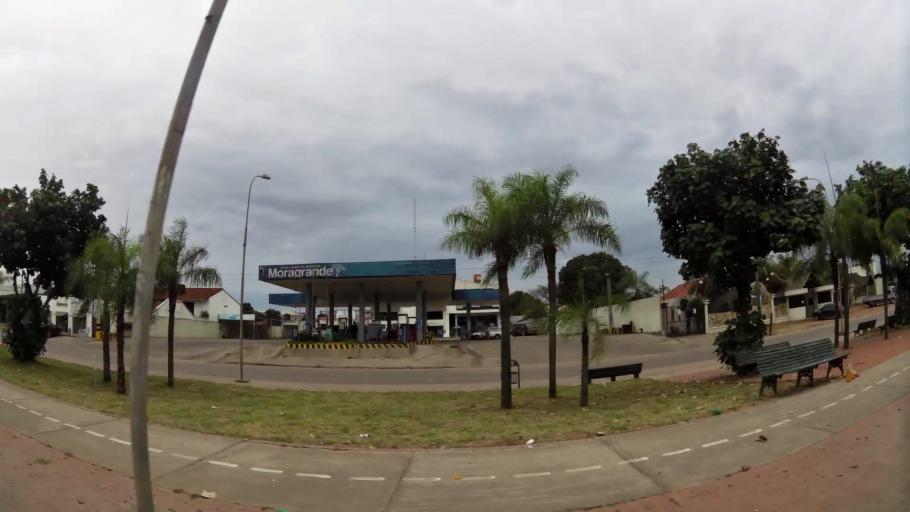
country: BO
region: Santa Cruz
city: Santa Cruz de la Sierra
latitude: -17.8316
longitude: -63.1857
